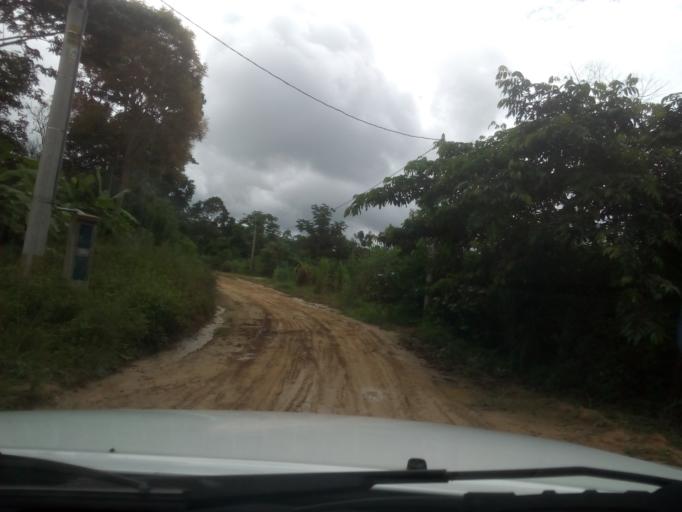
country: PE
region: San Martin
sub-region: Provincia de Lamas
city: Lamas
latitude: -6.4156
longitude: -76.4599
